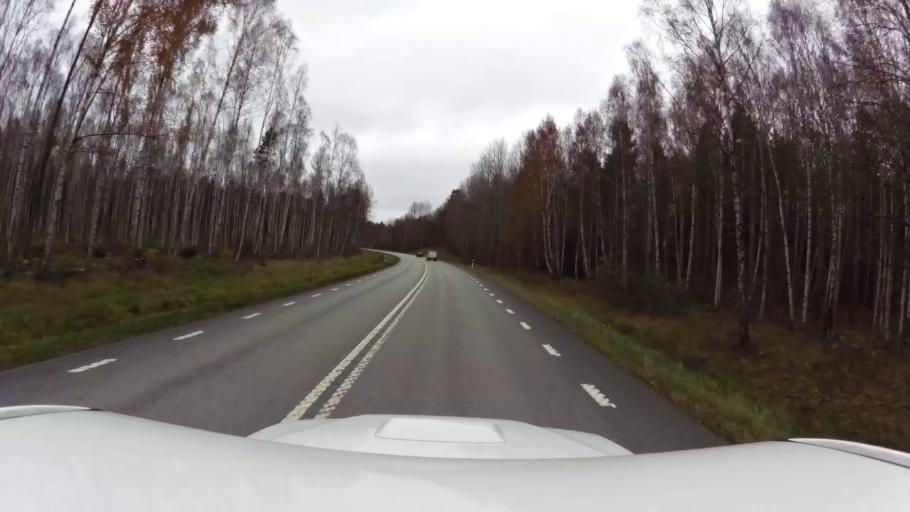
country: SE
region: OEstergoetland
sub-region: Kinda Kommun
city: Rimforsa
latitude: 58.1592
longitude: 15.6811
